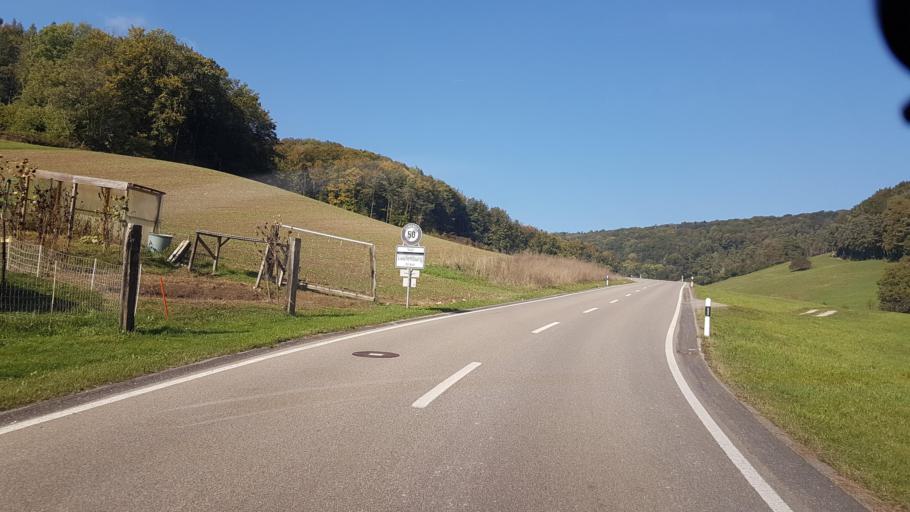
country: CH
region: Aargau
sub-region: Bezirk Laufenburg
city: Sulz
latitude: 47.5185
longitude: 8.1312
